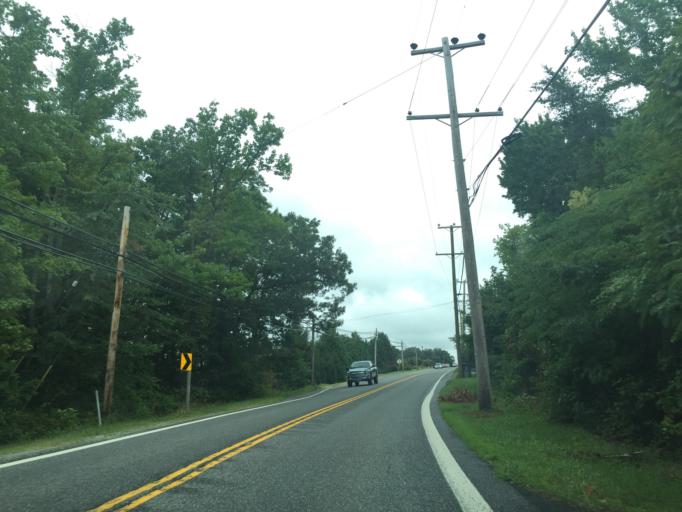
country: US
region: Maryland
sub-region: Harford County
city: Joppatowne
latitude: 39.4356
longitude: -76.3550
